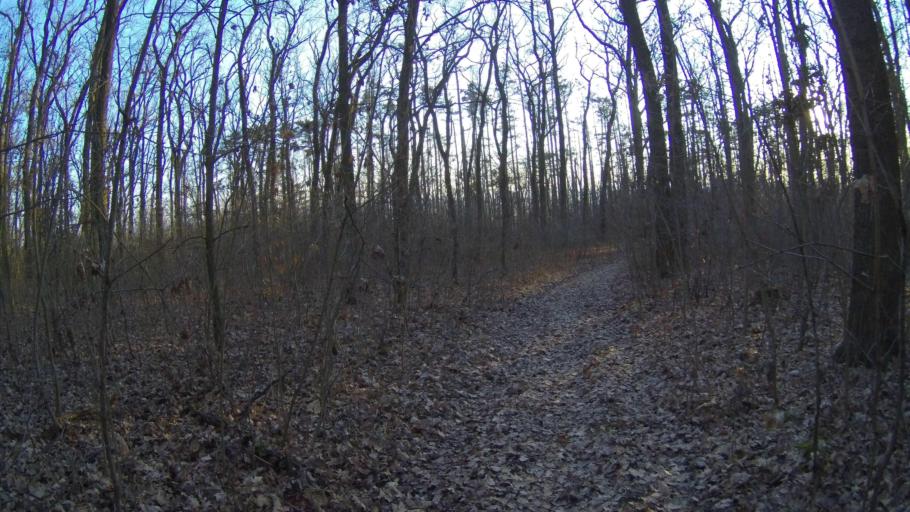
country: CZ
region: Ustecky
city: Roudnice nad Labem
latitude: 50.3820
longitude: 14.2851
